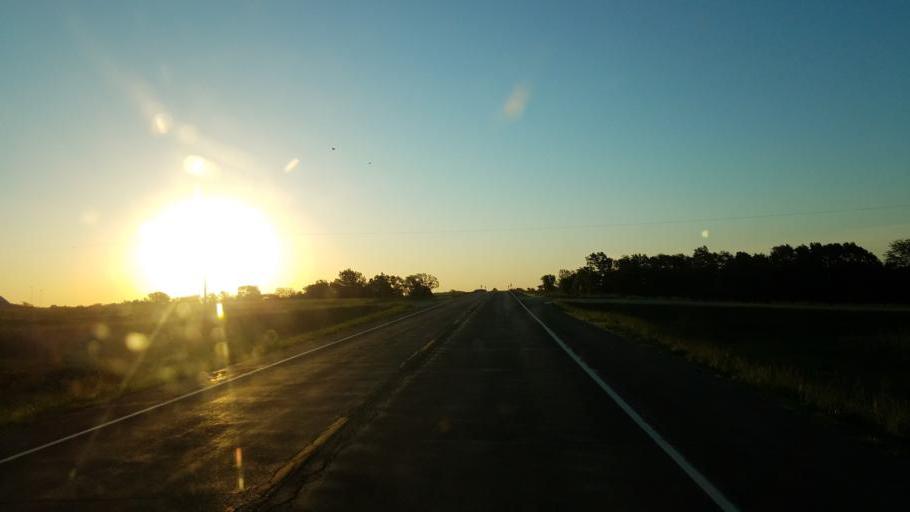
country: US
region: Missouri
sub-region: Schuyler County
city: Lancaster
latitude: 40.4927
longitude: -92.5814
